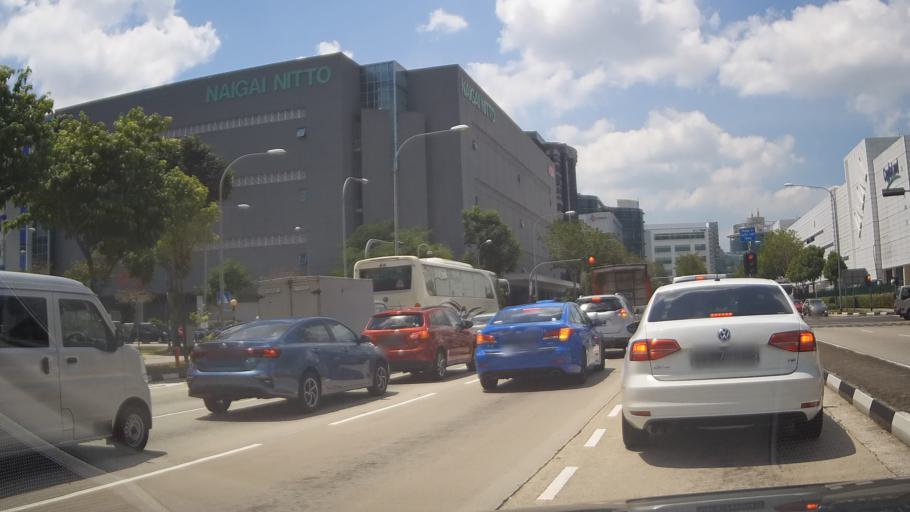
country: SG
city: Singapore
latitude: 1.3369
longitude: 103.7476
